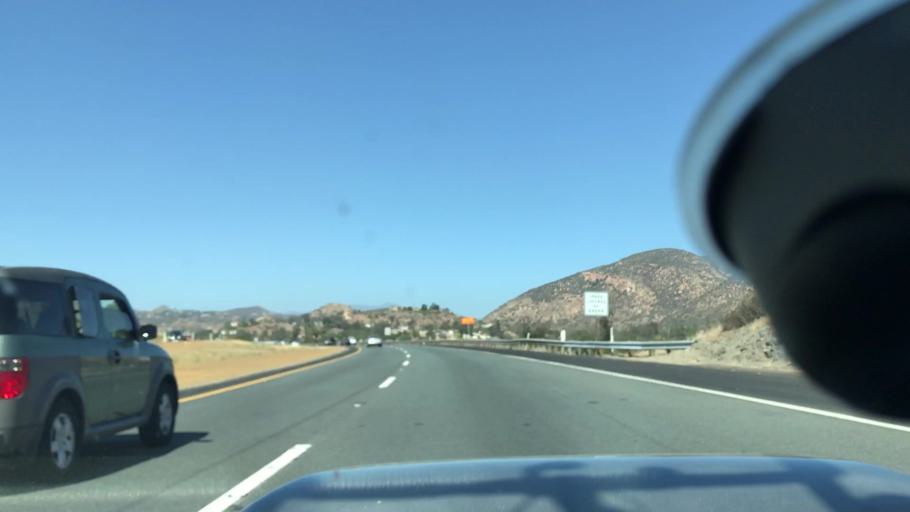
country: US
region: California
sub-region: San Diego County
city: Crest
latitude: 32.8455
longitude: -116.8773
